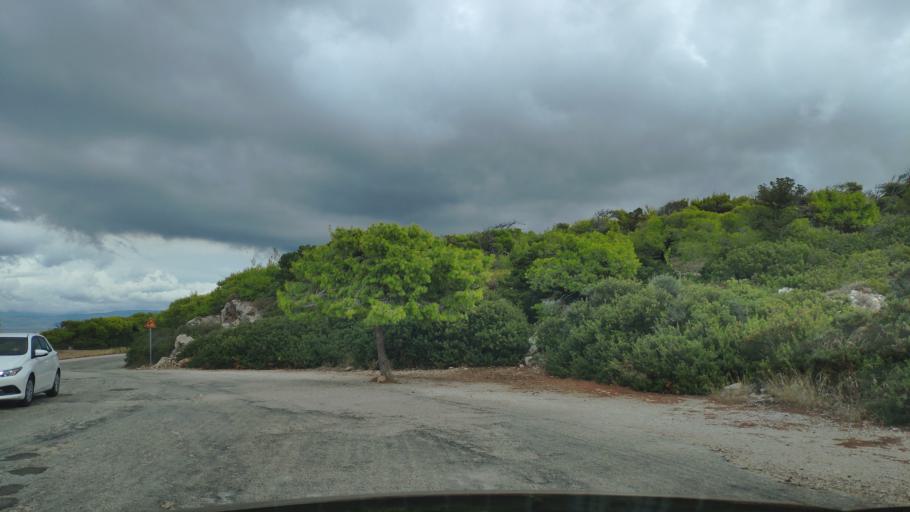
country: GR
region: Peloponnese
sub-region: Nomos Korinthias
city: Vrakhati
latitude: 38.0289
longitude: 22.8538
